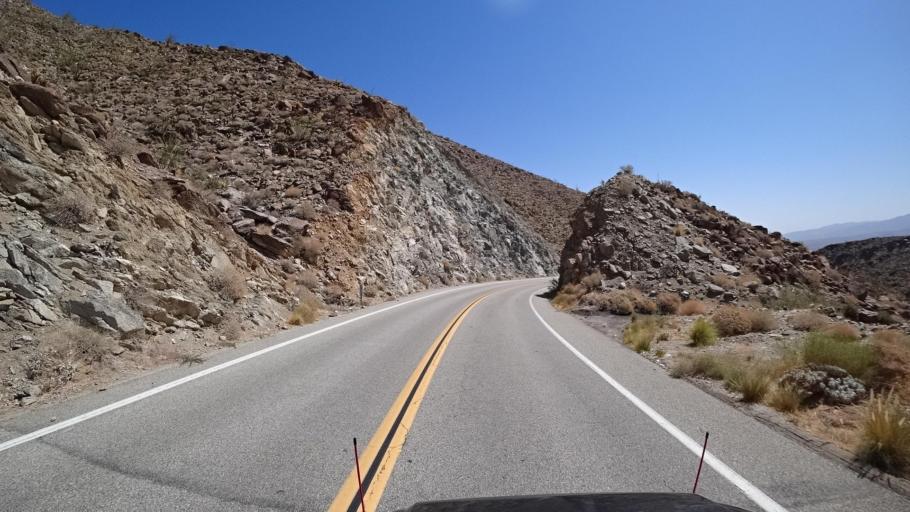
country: US
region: California
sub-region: San Diego County
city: Borrego Springs
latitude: 33.2254
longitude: -116.4188
